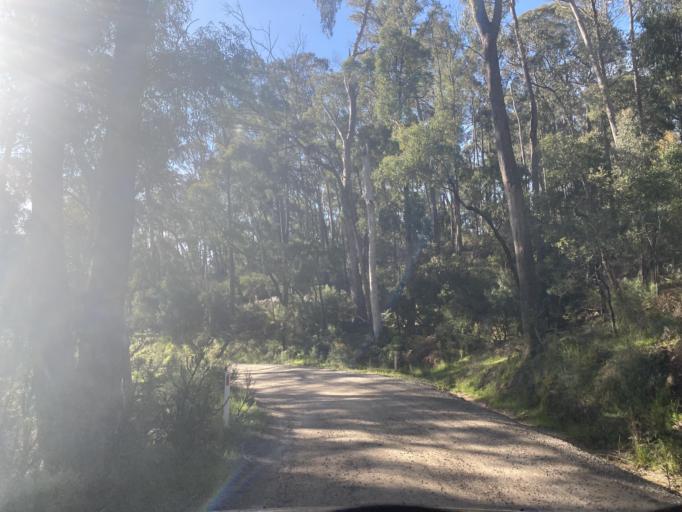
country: AU
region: Victoria
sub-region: Mansfield
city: Mansfield
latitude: -36.8268
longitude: 146.1421
